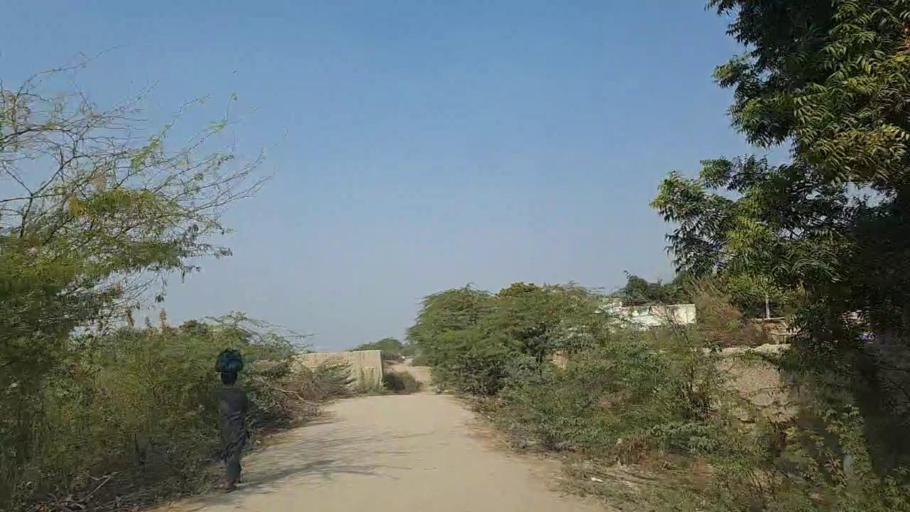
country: PK
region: Sindh
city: Daur
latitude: 26.4810
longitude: 68.4648
